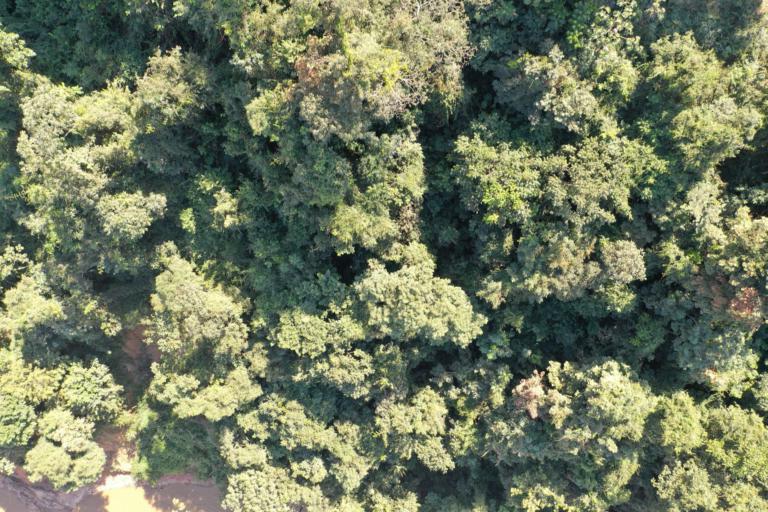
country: BO
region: La Paz
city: Mapiri
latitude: -15.3058
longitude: -68.2152
